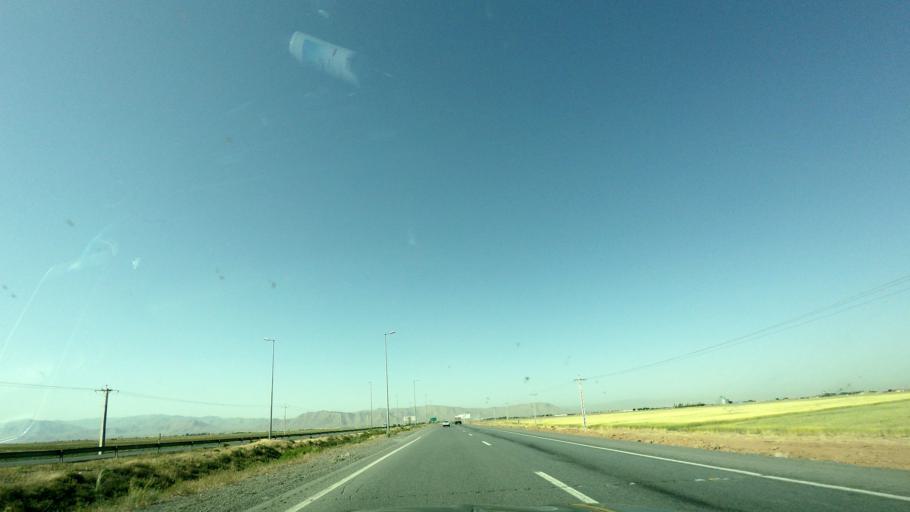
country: IR
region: Markazi
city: Ashtian
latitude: 34.1994
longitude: 50.0599
